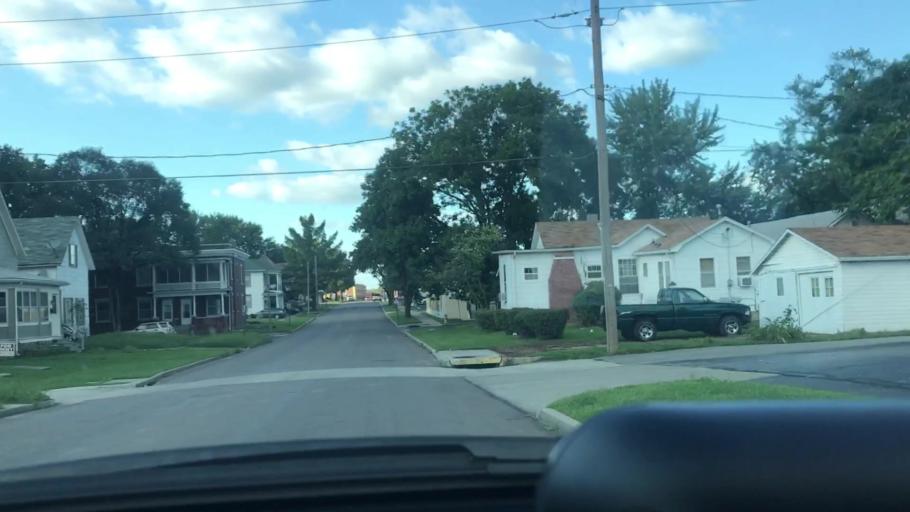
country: US
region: Missouri
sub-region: Pettis County
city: Sedalia
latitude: 38.7055
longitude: -93.2304
